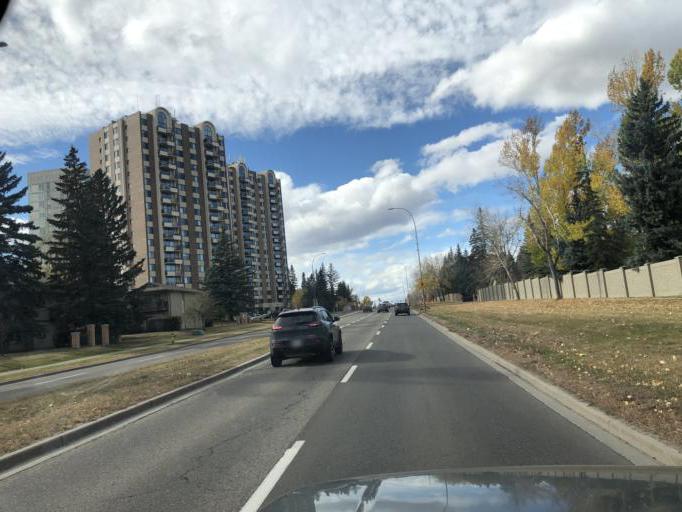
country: CA
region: Alberta
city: Calgary
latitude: 50.9723
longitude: -114.1069
